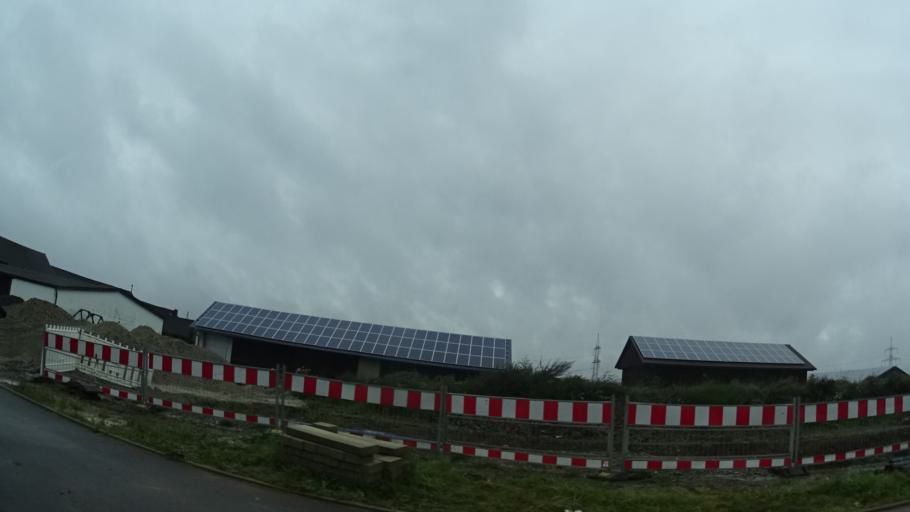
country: DE
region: Bavaria
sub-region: Upper Franconia
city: Tschirn
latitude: 50.3575
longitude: 11.4191
